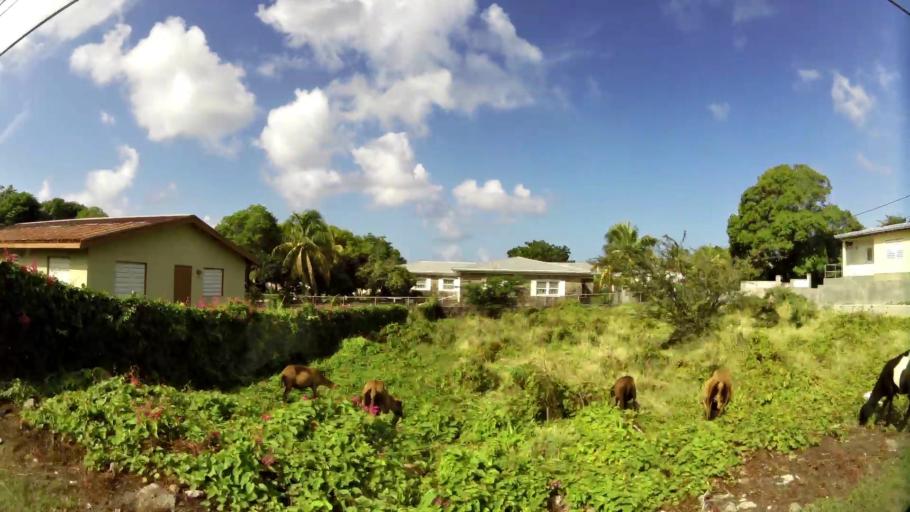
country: KN
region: Saint Paul Charlestown
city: Charlestown
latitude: 17.1346
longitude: -62.6186
